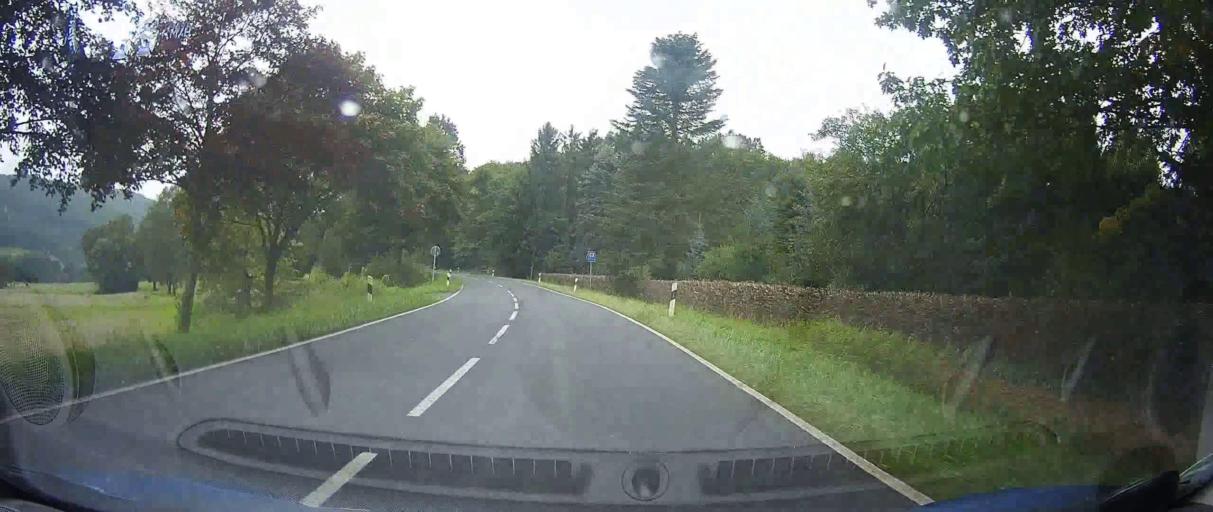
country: DE
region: Lower Saxony
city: Uslar
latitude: 51.6844
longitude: 9.6414
